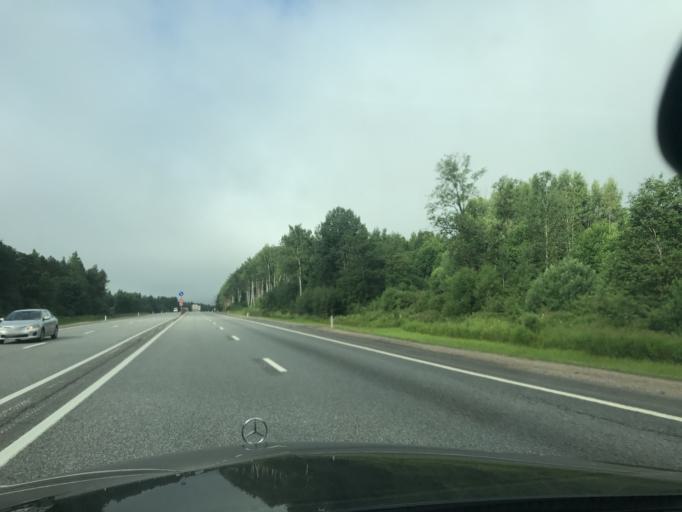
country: RU
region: Smolensk
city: Vyaz'ma
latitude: 55.3278
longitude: 34.5709
